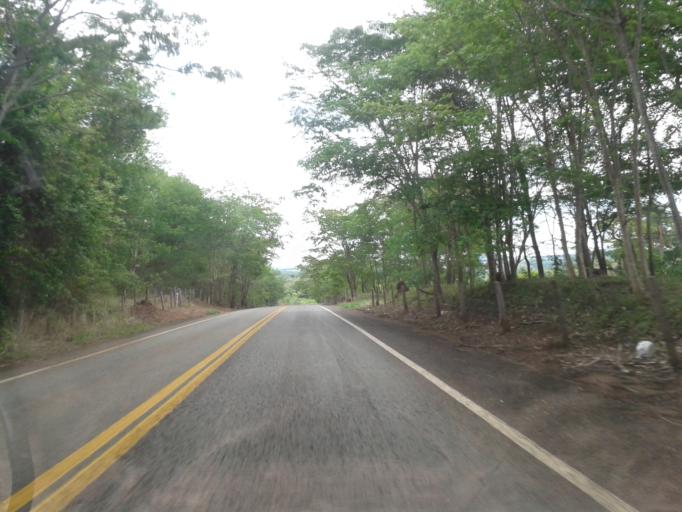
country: BR
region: Goias
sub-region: Buriti Alegre
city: Buriti Alegre
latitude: -18.1349
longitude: -49.1985
